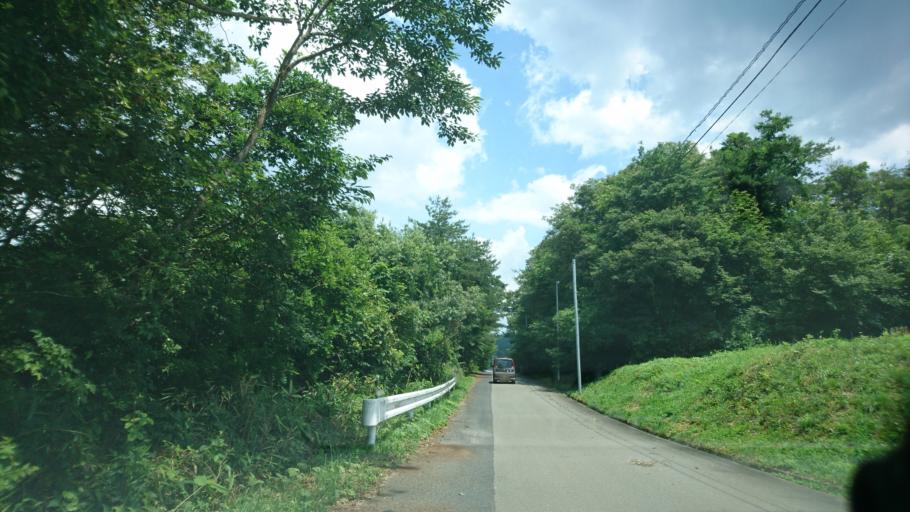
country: JP
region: Iwate
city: Ichinoseki
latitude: 38.9151
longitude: 141.2142
